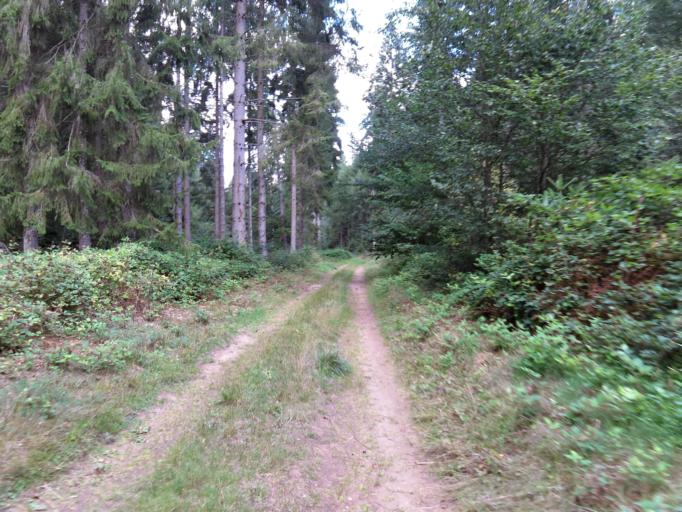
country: DE
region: Rheinland-Pfalz
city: Weidenthal
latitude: 49.4047
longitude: 7.9882
